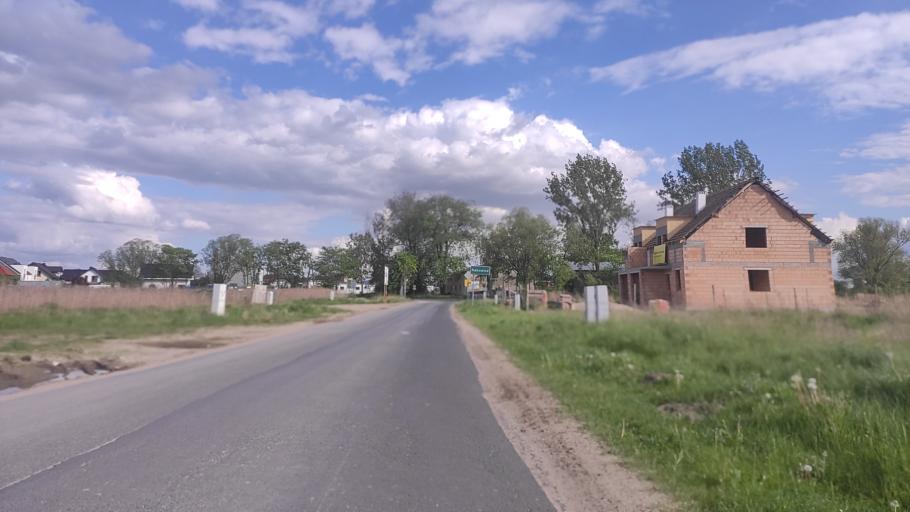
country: PL
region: Greater Poland Voivodeship
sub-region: Powiat poznanski
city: Swarzedz
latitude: 52.3912
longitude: 17.1185
